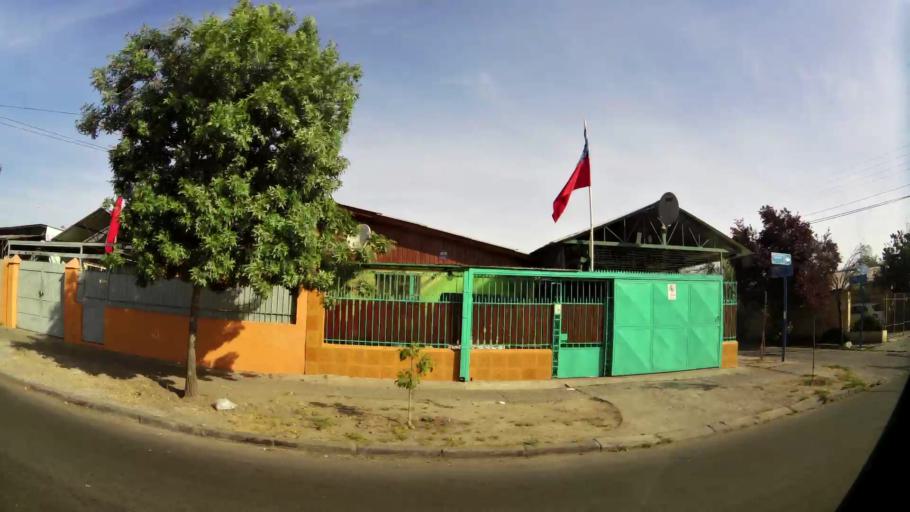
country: CL
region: Santiago Metropolitan
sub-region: Provincia de Santiago
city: La Pintana
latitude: -33.5210
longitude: -70.6339
